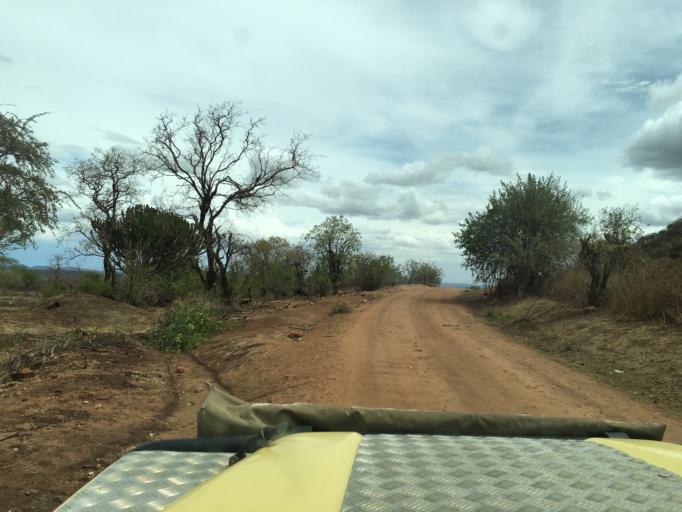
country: KE
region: Kajiado
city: Magadi
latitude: -2.2457
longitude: 35.6770
